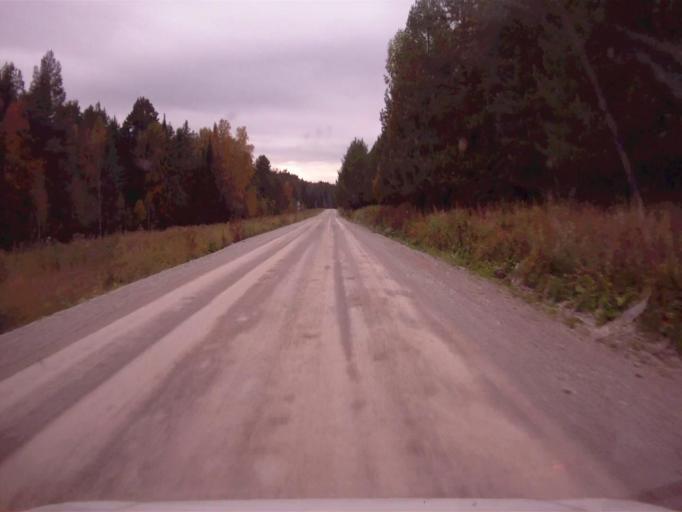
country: RU
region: Chelyabinsk
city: Nyazepetrovsk
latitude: 56.0481
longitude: 59.5272
